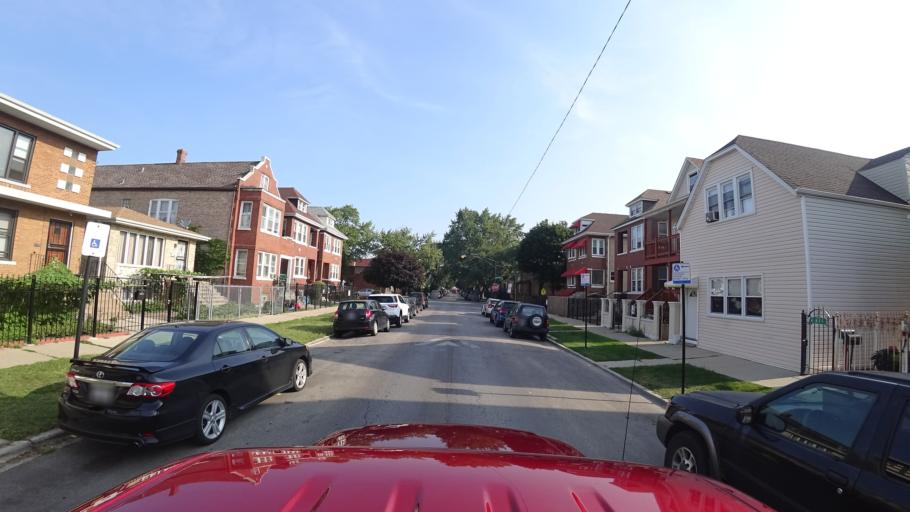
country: US
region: Illinois
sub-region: Cook County
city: Cicero
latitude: 41.8113
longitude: -87.7017
